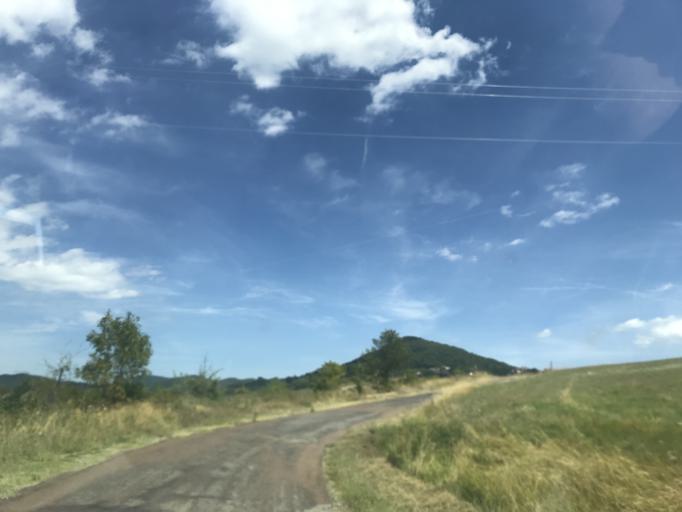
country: IT
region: Emilia-Romagna
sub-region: Provincia di Bologna
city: Vergato
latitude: 44.2448
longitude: 11.1132
